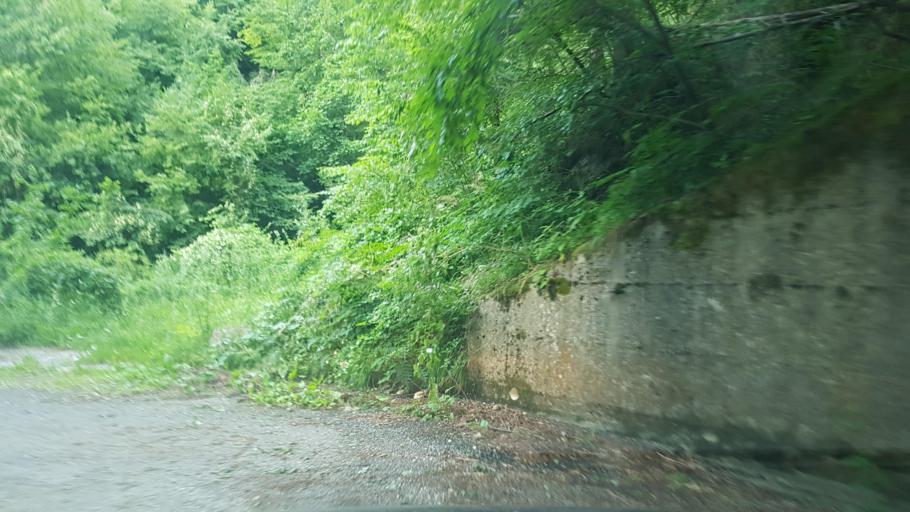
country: IT
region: Friuli Venezia Giulia
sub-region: Provincia di Udine
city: Paularo
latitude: 46.4799
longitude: 13.0985
